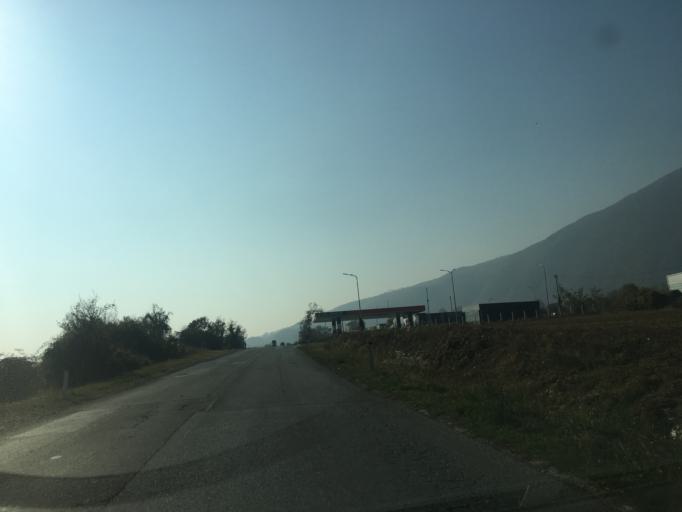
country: XK
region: Gjakova
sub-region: Komuna e Decanit
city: Strellc i Eperm
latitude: 42.6046
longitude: 20.3015
